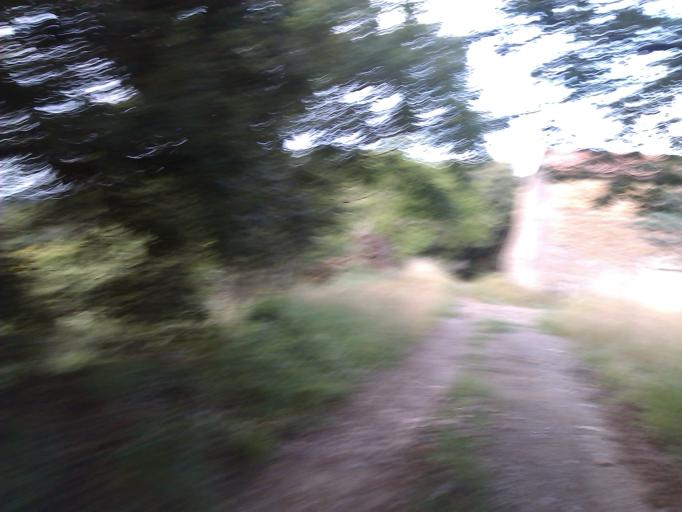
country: IT
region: Tuscany
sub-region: Province of Arezzo
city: Ponticino
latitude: 43.4592
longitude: 11.7401
